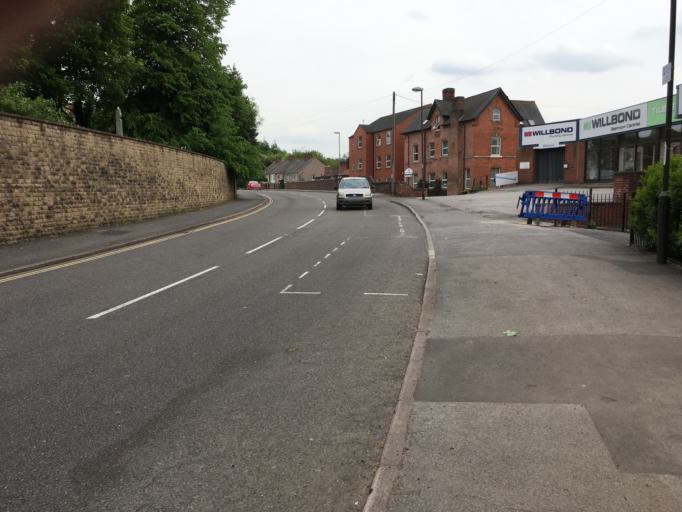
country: GB
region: England
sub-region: Derbyshire
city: Chesterfield
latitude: 53.2320
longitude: -1.4182
